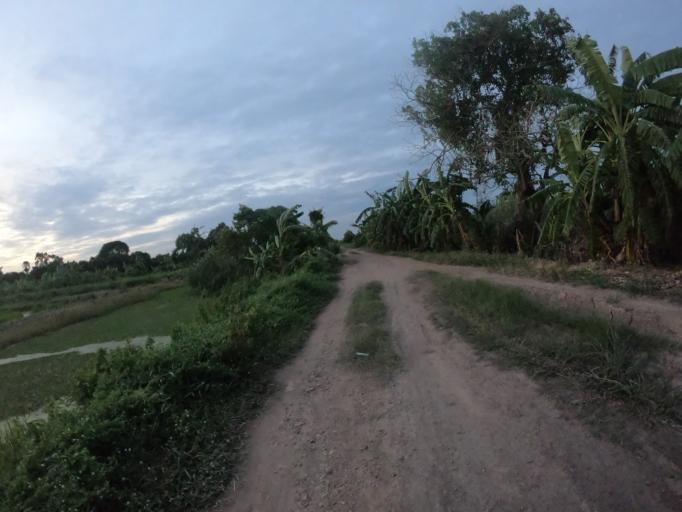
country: TH
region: Pathum Thani
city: Ban Rangsit
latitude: 14.0251
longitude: 100.8019
